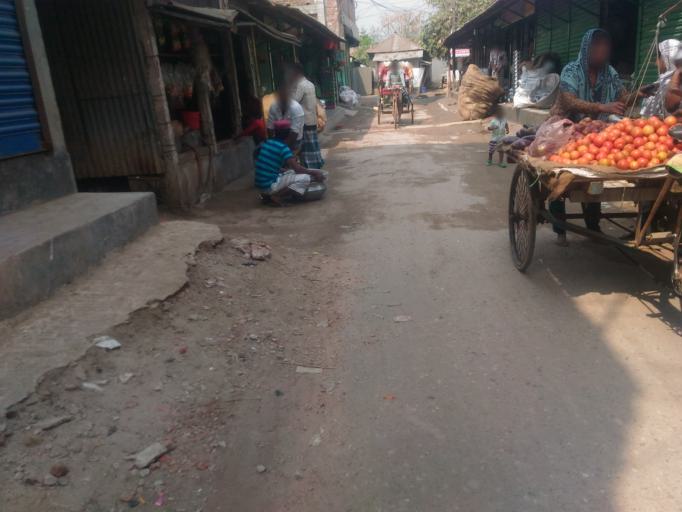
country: BD
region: Dhaka
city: Tungi
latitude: 23.9932
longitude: 90.3772
